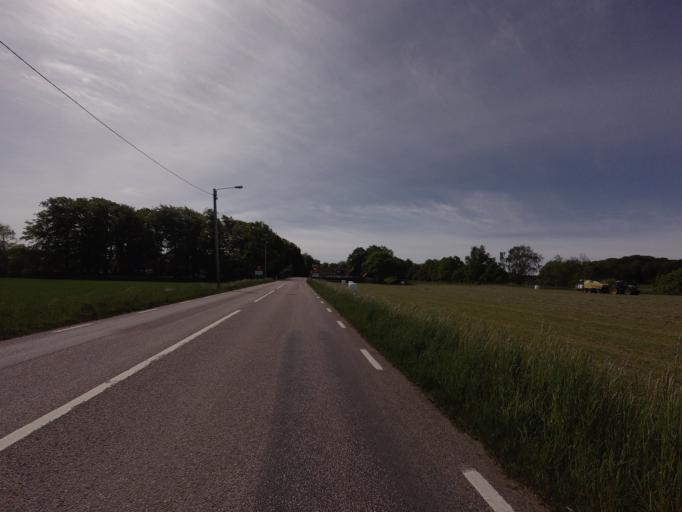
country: SE
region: Skane
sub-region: Helsingborg
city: Odakra
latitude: 56.1332
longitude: 12.6916
